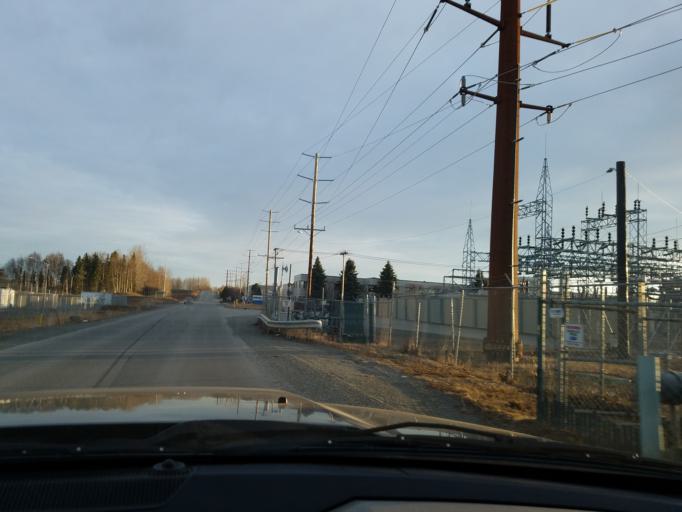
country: US
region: Alaska
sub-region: Anchorage Municipality
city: Anchorage
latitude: 61.1685
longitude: -149.9128
